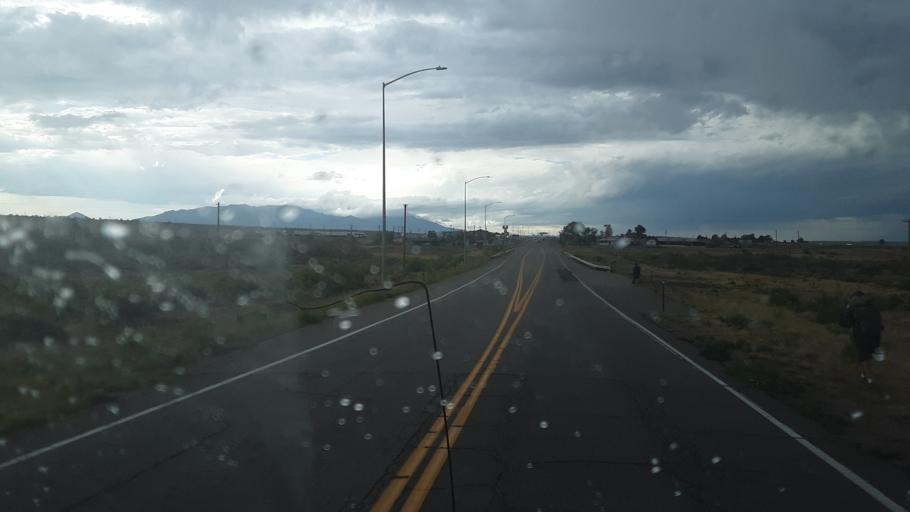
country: US
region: Colorado
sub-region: Huerfano County
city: Walsenburg
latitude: 37.6487
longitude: -104.7906
